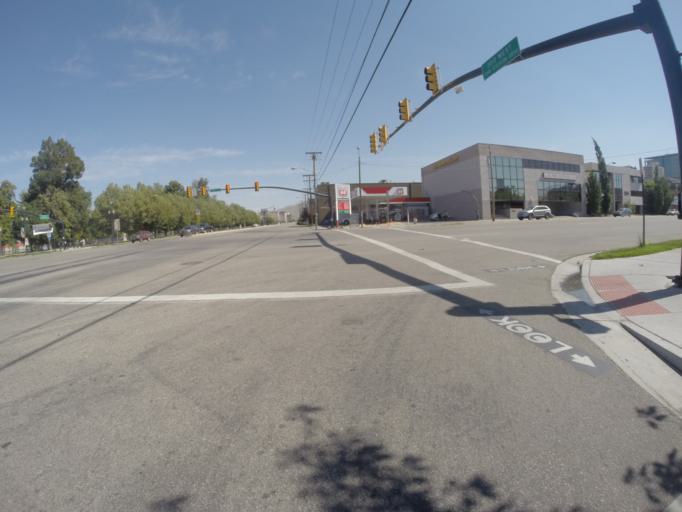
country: US
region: Utah
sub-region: Salt Lake County
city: Salt Lake City
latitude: 40.7604
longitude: -111.8995
